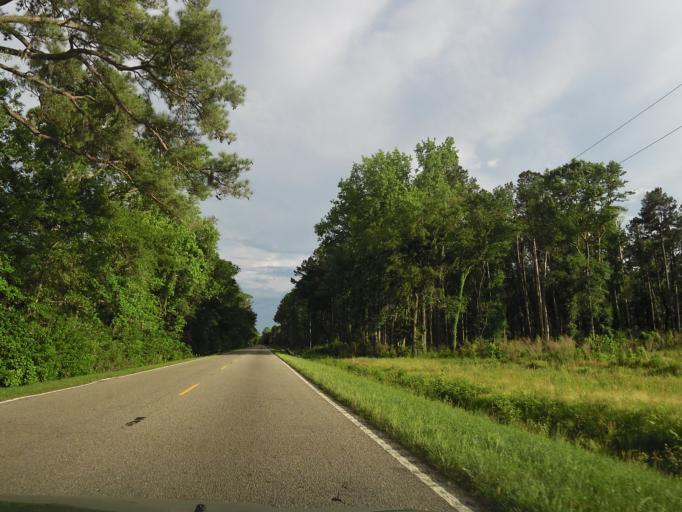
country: US
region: South Carolina
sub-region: Jasper County
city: Ridgeland
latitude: 32.5195
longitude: -81.1472
